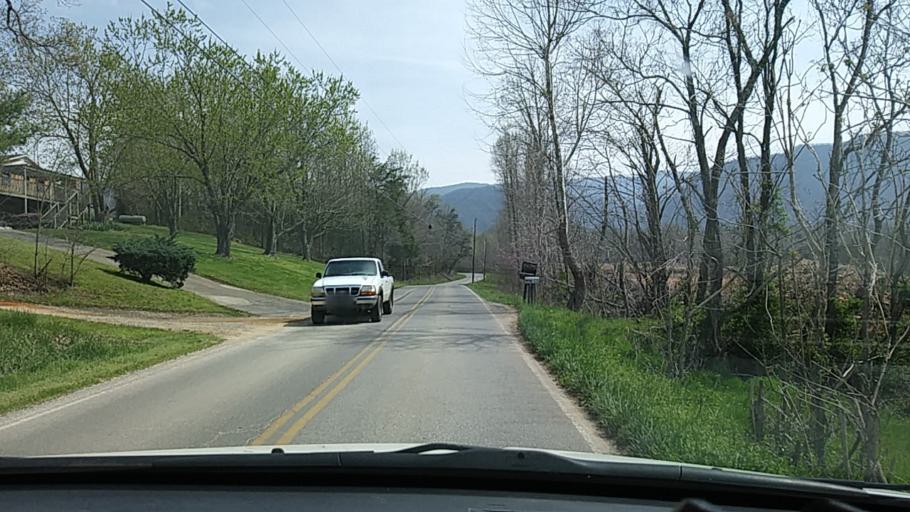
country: US
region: Tennessee
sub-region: Greene County
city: Tusculum
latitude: 36.0902
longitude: -82.7272
